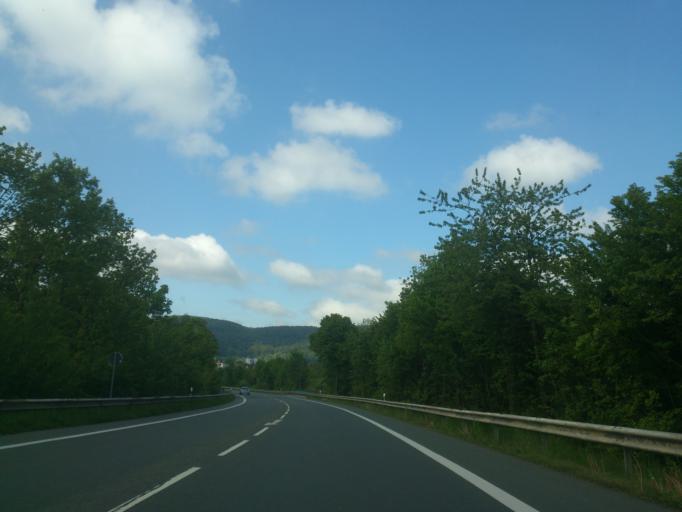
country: DE
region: North Rhine-Westphalia
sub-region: Regierungsbezirk Detmold
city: Bad Driburg
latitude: 51.7254
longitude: 9.0322
